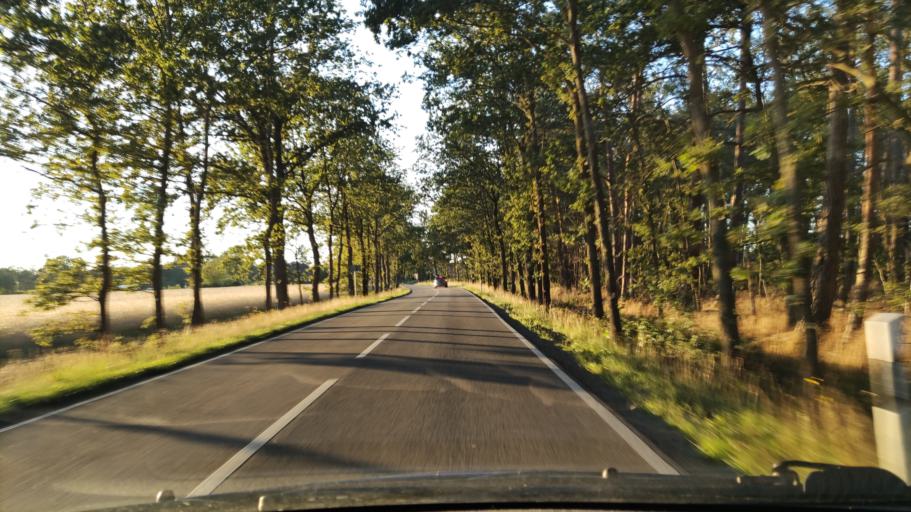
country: DE
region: Lower Saxony
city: Klein Gusborn
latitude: 53.0444
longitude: 11.1768
